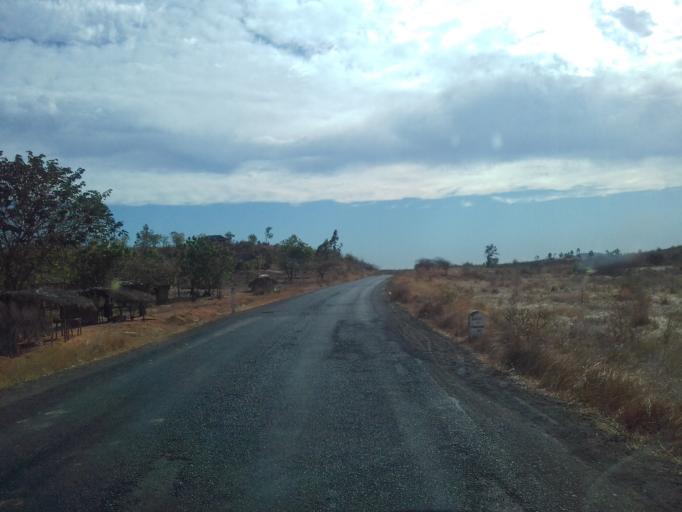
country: MG
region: Sofia
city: Antsohihy
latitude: -15.3779
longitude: 47.7383
